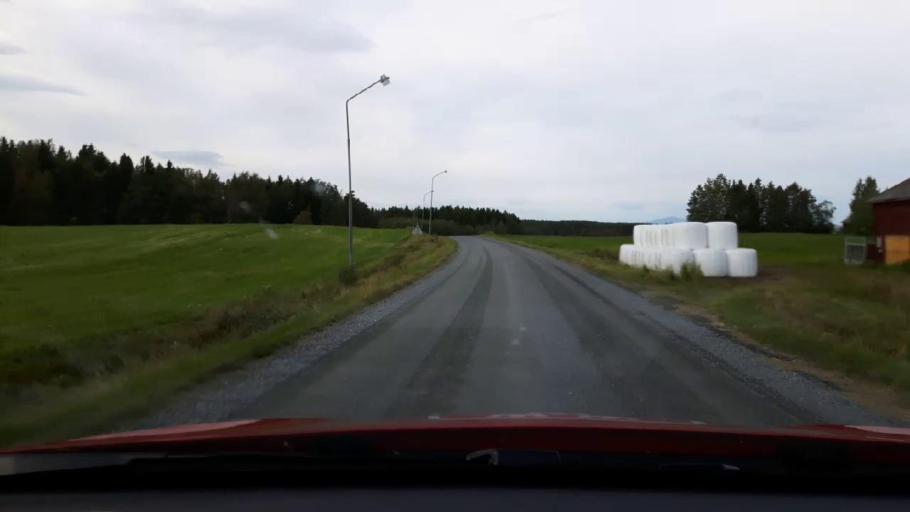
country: SE
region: Jaemtland
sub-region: Krokoms Kommun
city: Valla
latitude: 63.2437
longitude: 13.9915
